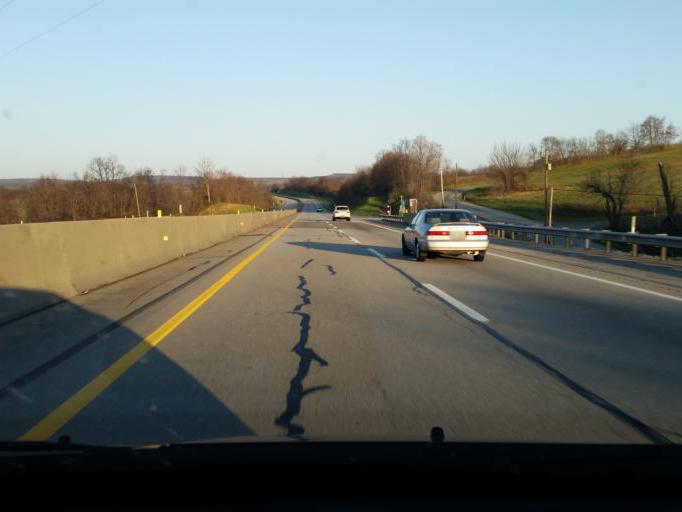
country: US
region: Pennsylvania
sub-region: Westmoreland County
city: Mount Pleasant
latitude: 40.1806
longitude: -79.5232
